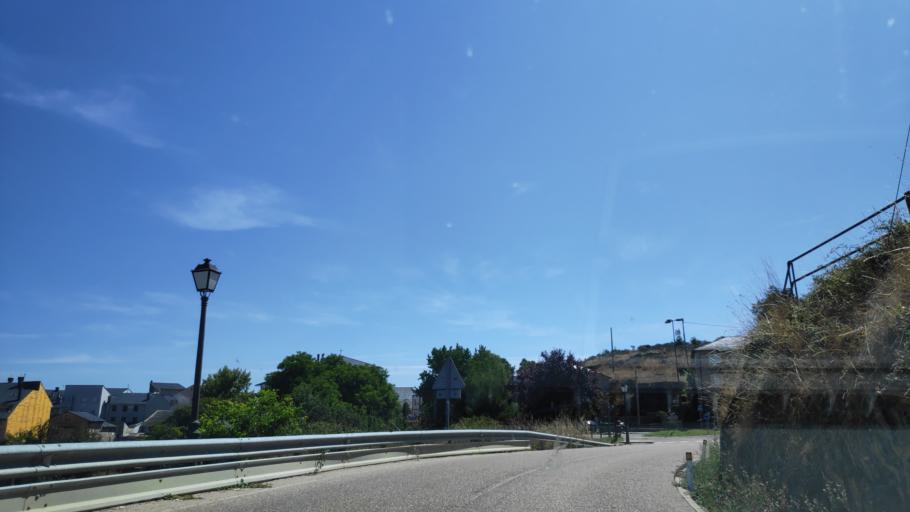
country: ES
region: Castille and Leon
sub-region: Provincia de Zamora
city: Puebla de Sanabria
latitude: 42.0515
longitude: -6.6361
